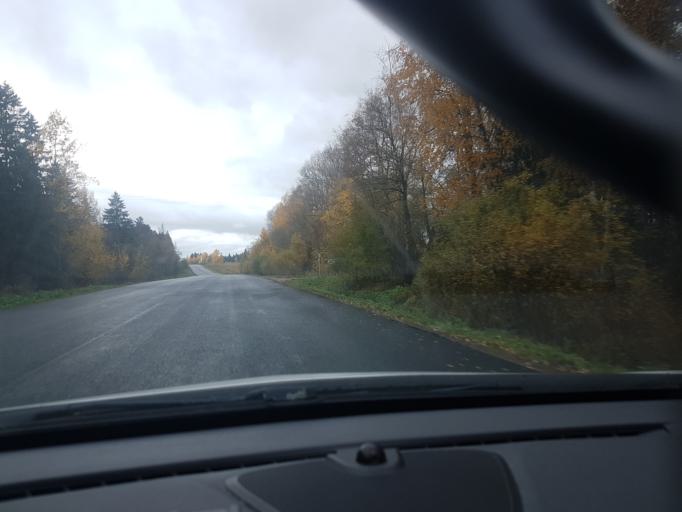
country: RU
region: Moskovskaya
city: Sychevo
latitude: 56.0040
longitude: 36.3083
